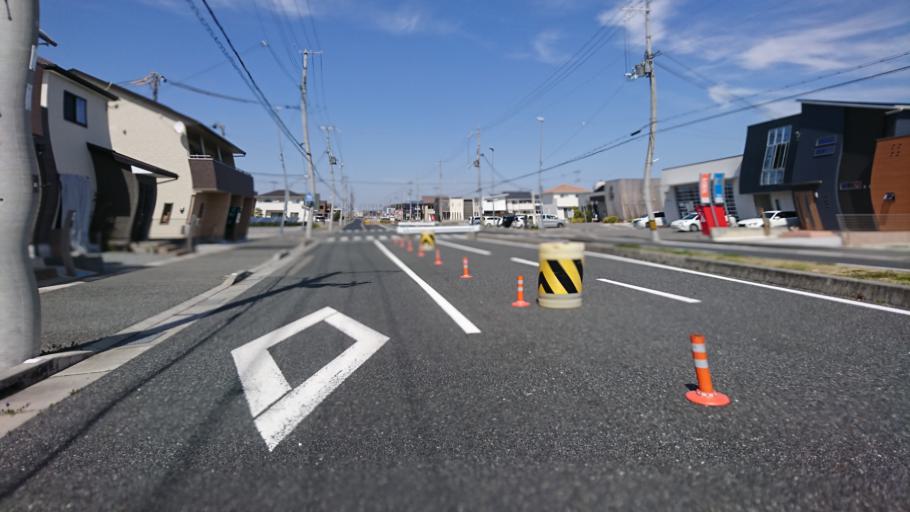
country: JP
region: Hyogo
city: Kakogawacho-honmachi
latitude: 34.7432
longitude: 134.9134
